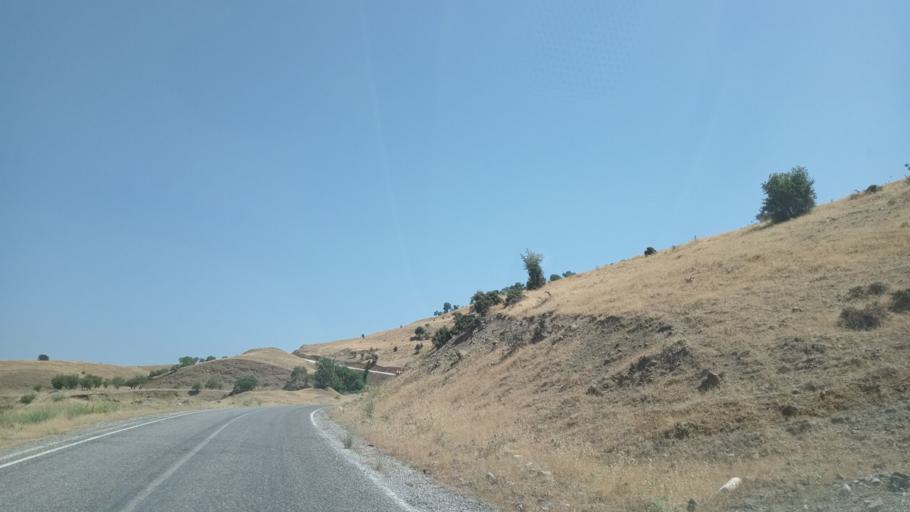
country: TR
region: Siirt
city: Dilektepe
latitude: 38.0697
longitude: 41.8296
